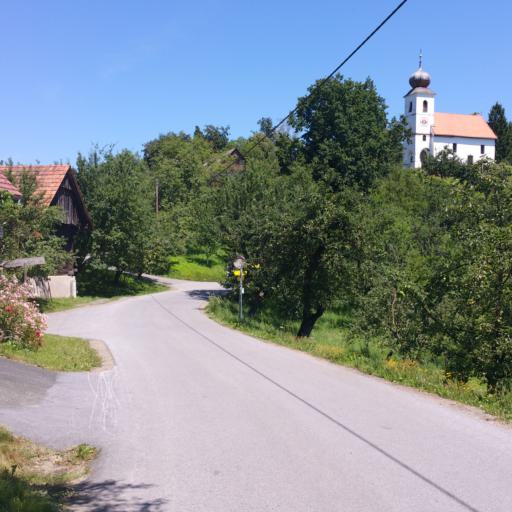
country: AT
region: Styria
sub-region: Politischer Bezirk Leibnitz
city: Gleinstatten
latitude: 46.7327
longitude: 15.3588
